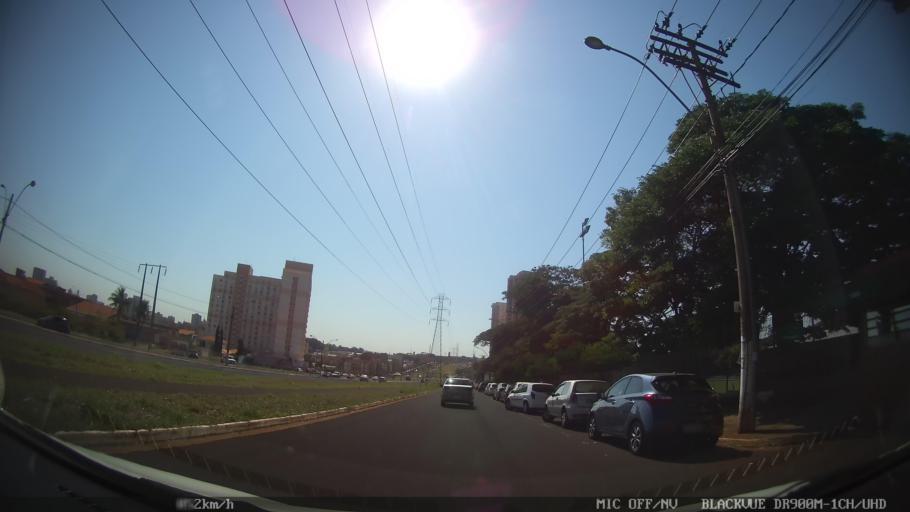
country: BR
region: Sao Paulo
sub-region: Ribeirao Preto
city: Ribeirao Preto
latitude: -21.2004
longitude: -47.7802
